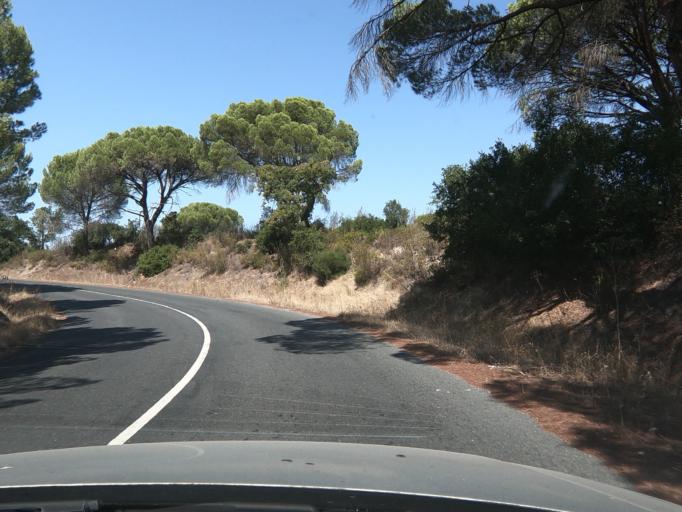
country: PT
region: Setubal
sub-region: Alcacer do Sal
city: Alcacer do Sal
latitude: 38.3117
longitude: -8.4322
